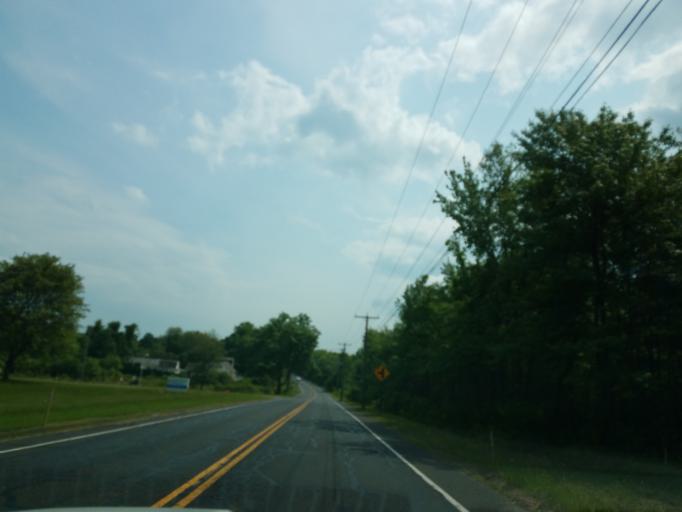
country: US
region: Massachusetts
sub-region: Hampden County
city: Agawam
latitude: 42.0362
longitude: -72.6368
